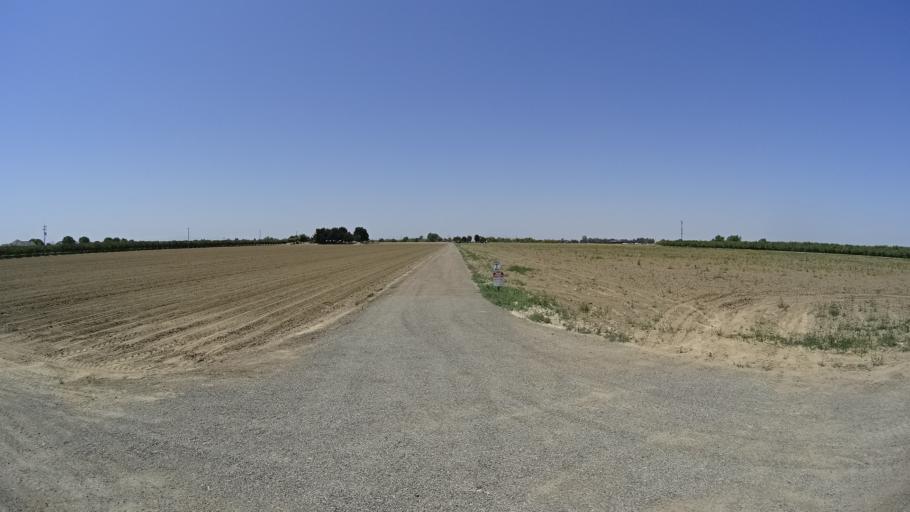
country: US
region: California
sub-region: Kings County
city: Lemoore
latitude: 36.2620
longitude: -119.7630
